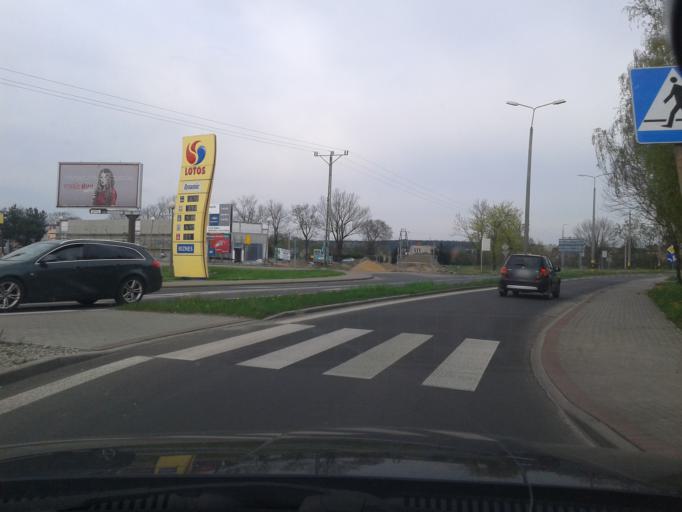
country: PL
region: Silesian Voivodeship
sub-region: Rybnik
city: Rybnik
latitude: 50.0903
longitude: 18.5760
